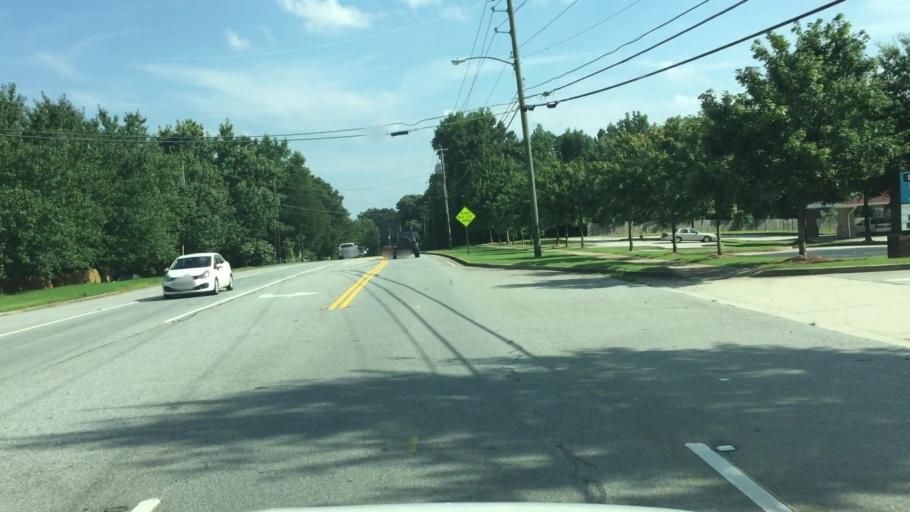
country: US
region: Georgia
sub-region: Gwinnett County
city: Dacula
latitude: 33.9802
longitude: -83.8940
